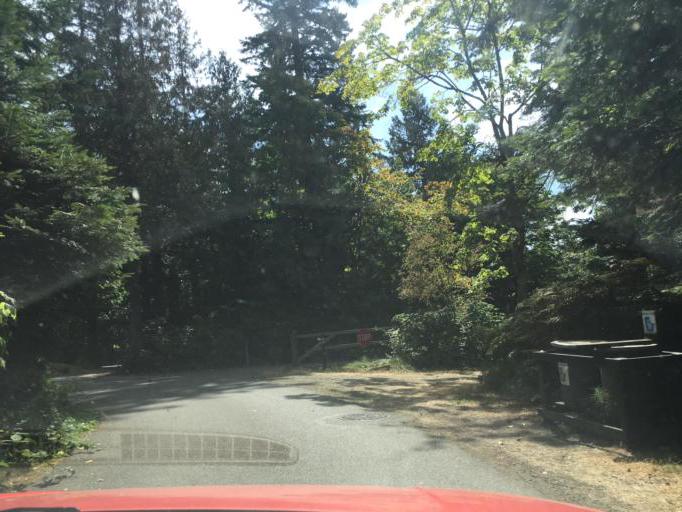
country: US
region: Washington
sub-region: Whatcom County
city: Bellingham
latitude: 48.6547
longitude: -122.4916
